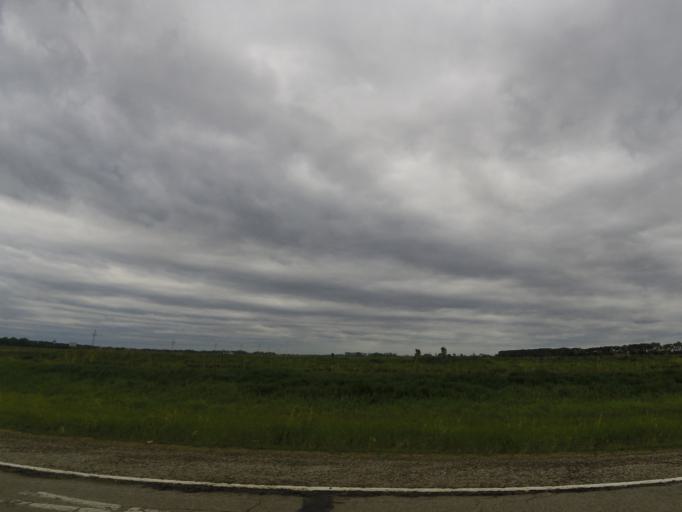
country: US
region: North Dakota
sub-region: Walsh County
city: Grafton
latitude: 48.5712
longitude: -97.4479
